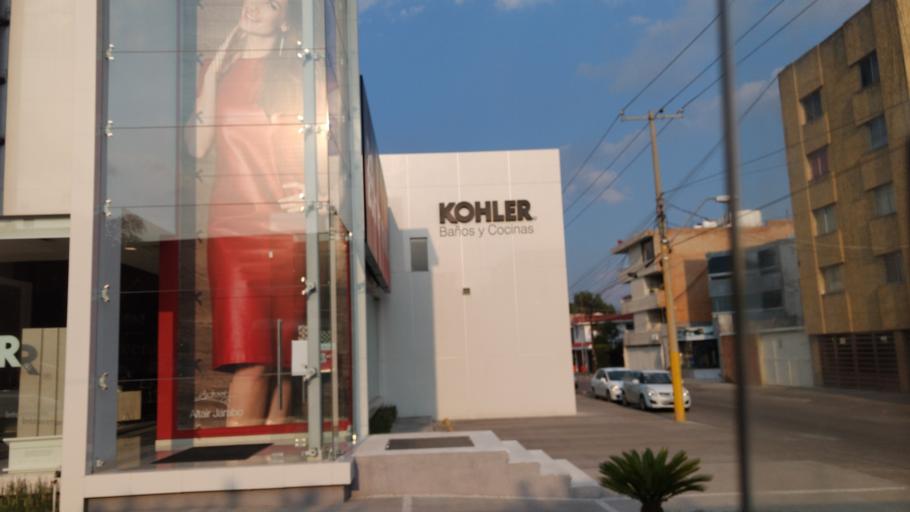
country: MX
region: Guanajuato
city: Leon
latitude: 21.1510
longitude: -101.6939
